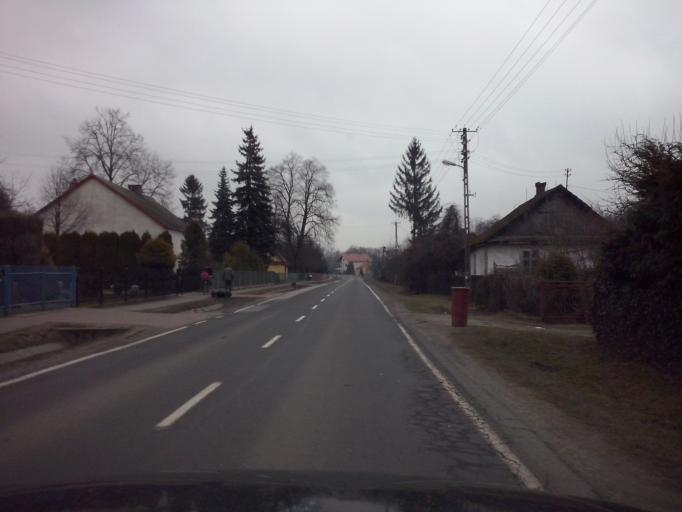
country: PL
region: Subcarpathian Voivodeship
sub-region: Powiat nizanski
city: Zarzecze
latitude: 50.5205
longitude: 22.2093
